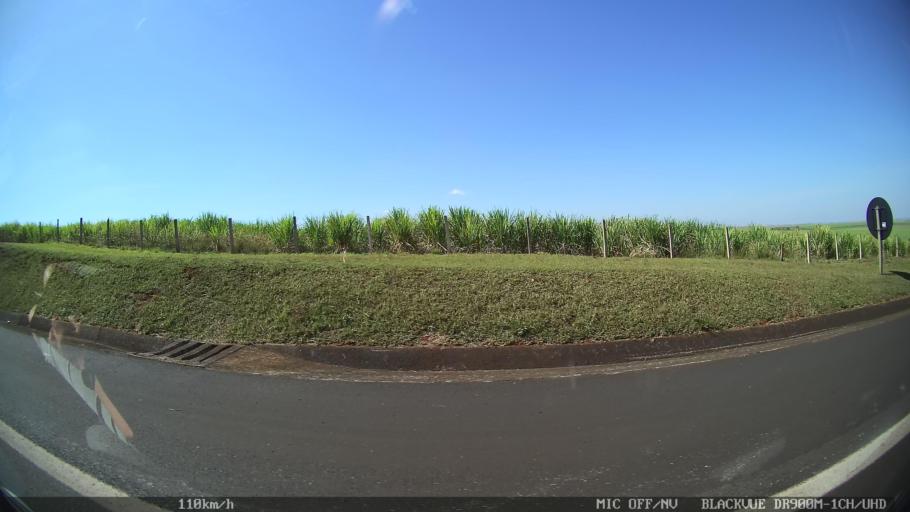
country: BR
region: Sao Paulo
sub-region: Franca
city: Franca
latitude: -20.6824
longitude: -47.4962
